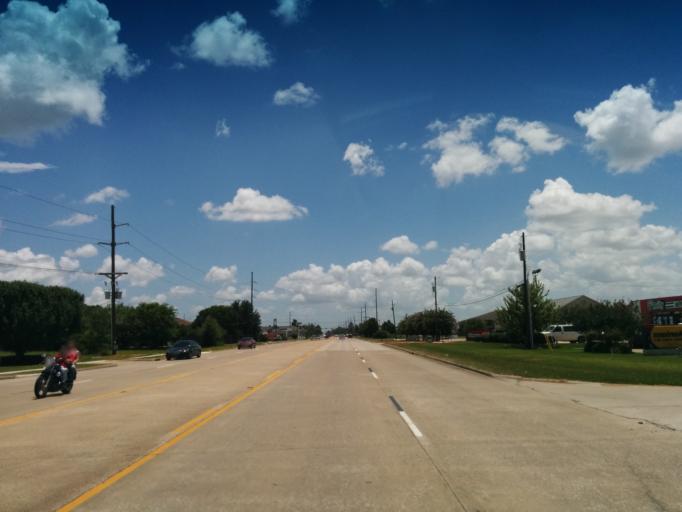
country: US
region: Texas
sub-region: Jefferson County
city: Beaumont
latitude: 30.0948
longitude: -94.1899
